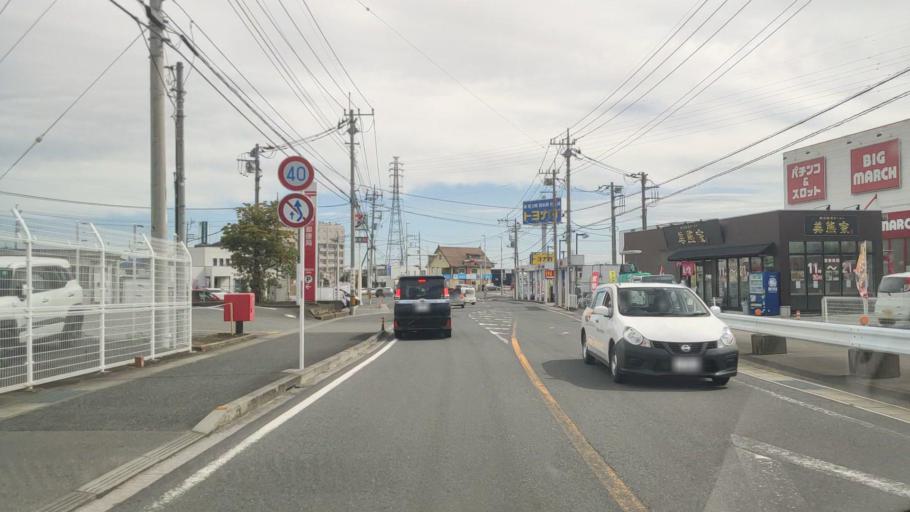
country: JP
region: Gunma
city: Takasaki
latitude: 36.3596
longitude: 139.0112
